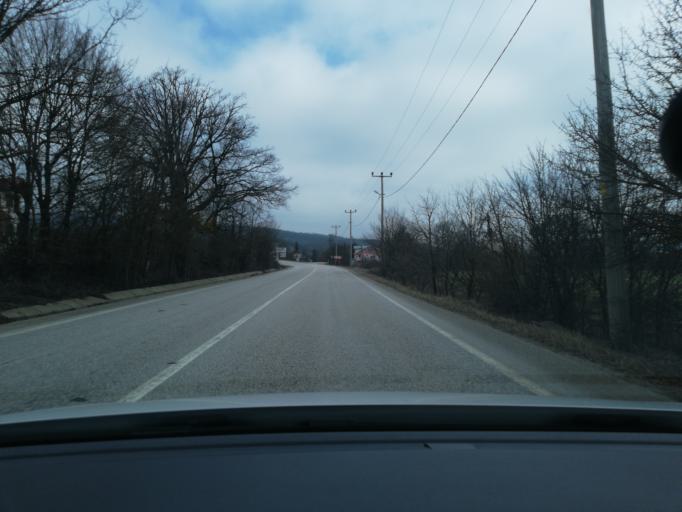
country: TR
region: Bolu
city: Bolu
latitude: 40.7116
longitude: 31.4698
